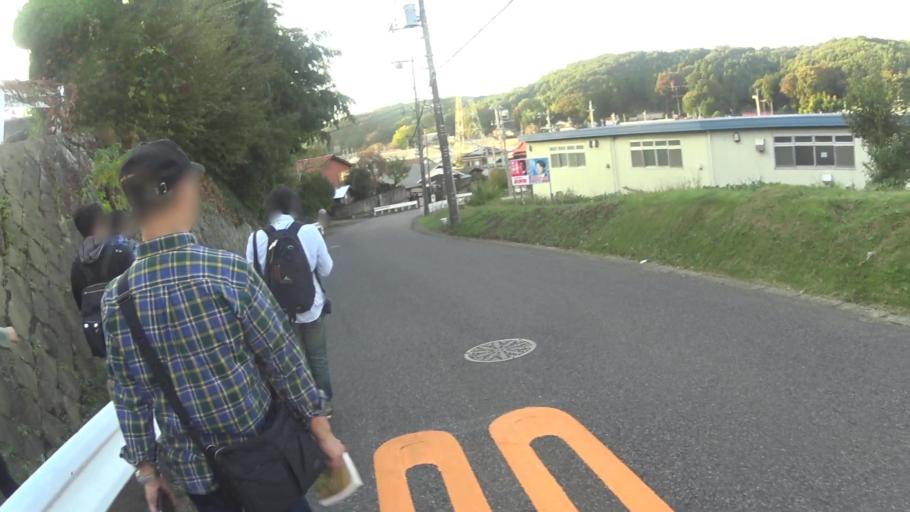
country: JP
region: Tokyo
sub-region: Machida-shi
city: Machida
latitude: 35.5857
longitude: 139.4479
